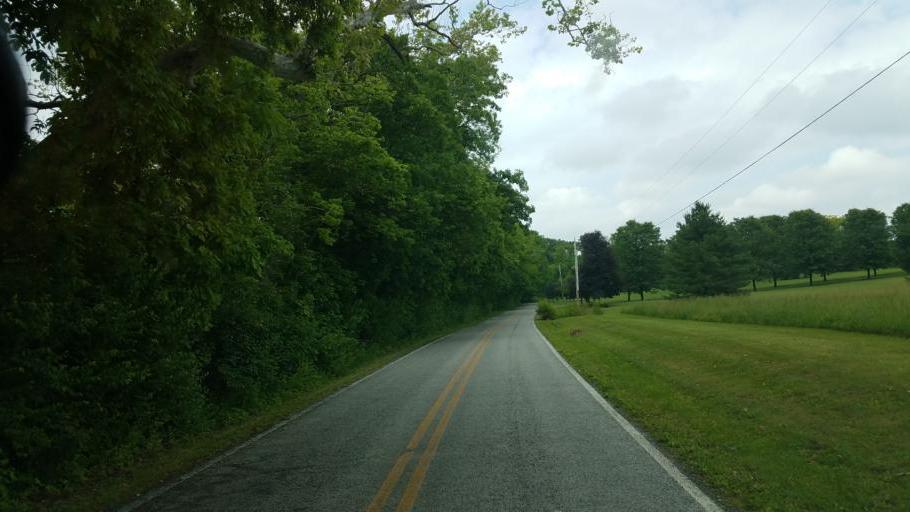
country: US
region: Ohio
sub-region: Delaware County
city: Delaware
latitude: 40.3320
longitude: -83.1730
